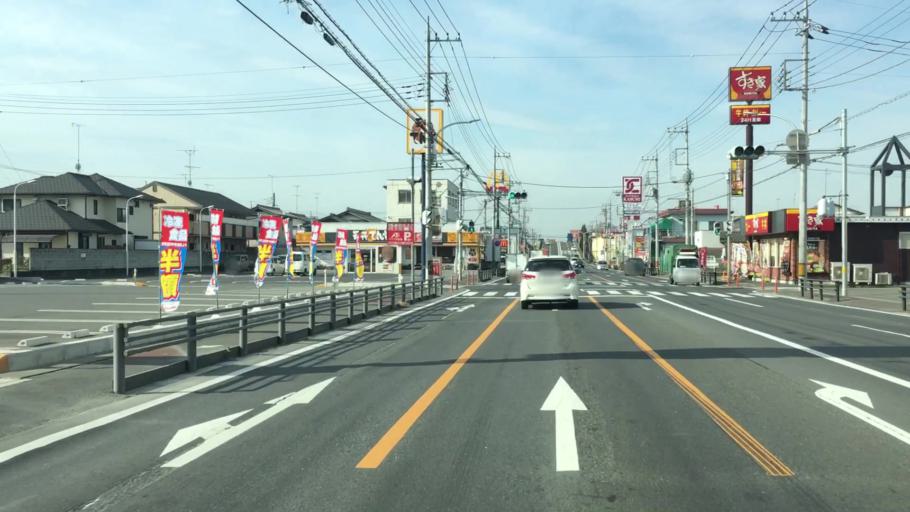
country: JP
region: Gunma
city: Tatebayashi
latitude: 36.2355
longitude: 139.5316
